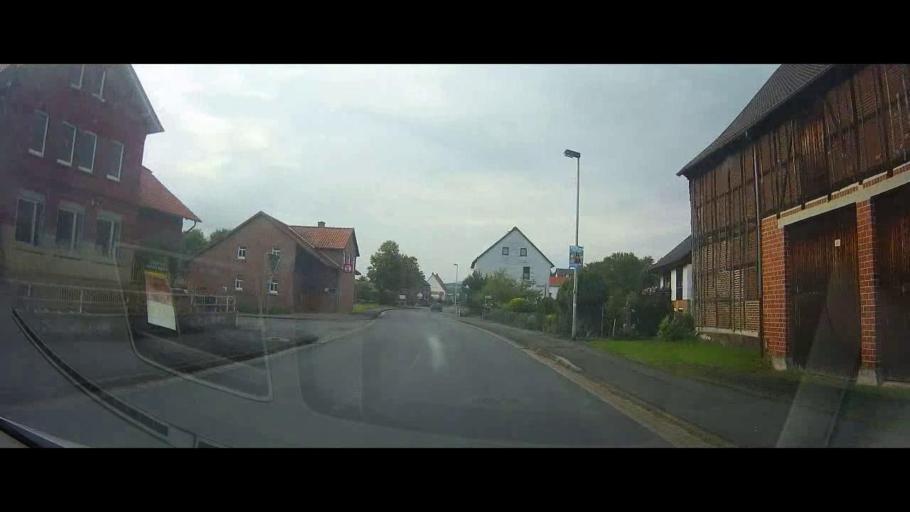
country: DE
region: Lower Saxony
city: Uslar
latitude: 51.6048
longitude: 9.6750
